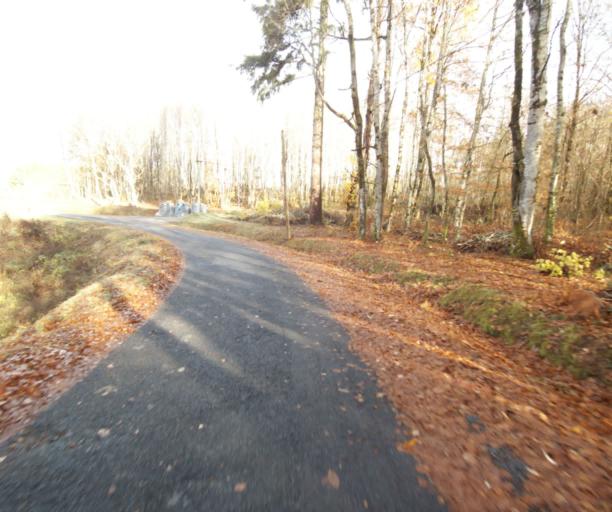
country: FR
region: Limousin
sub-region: Departement de la Correze
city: Sainte-Fortunade
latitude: 45.2190
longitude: 1.7485
